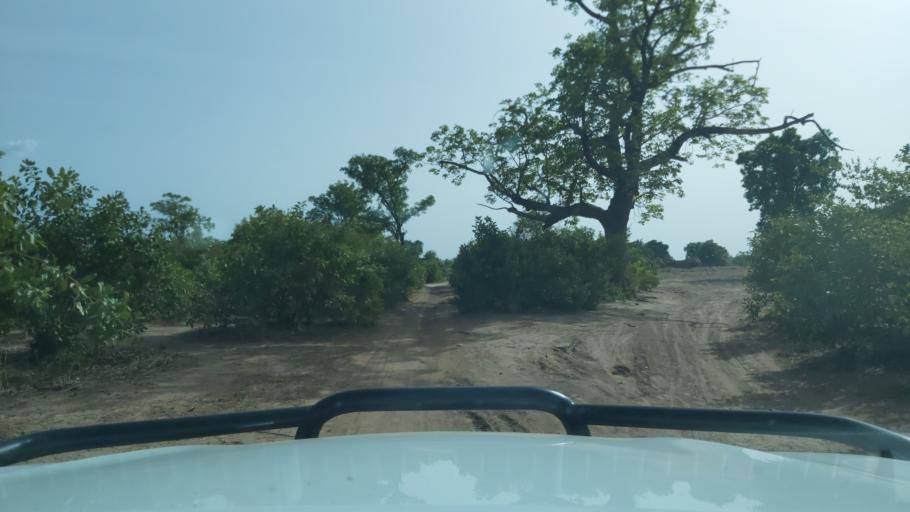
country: ML
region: Koulikoro
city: Koulikoro
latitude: 13.1763
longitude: -7.7539
